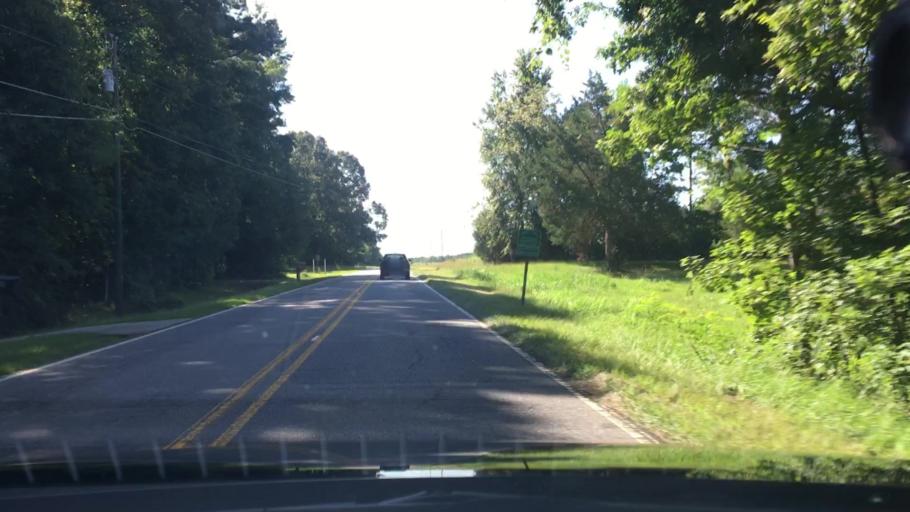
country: US
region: Georgia
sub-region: Putnam County
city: Jefferson
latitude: 33.3967
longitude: -83.2711
